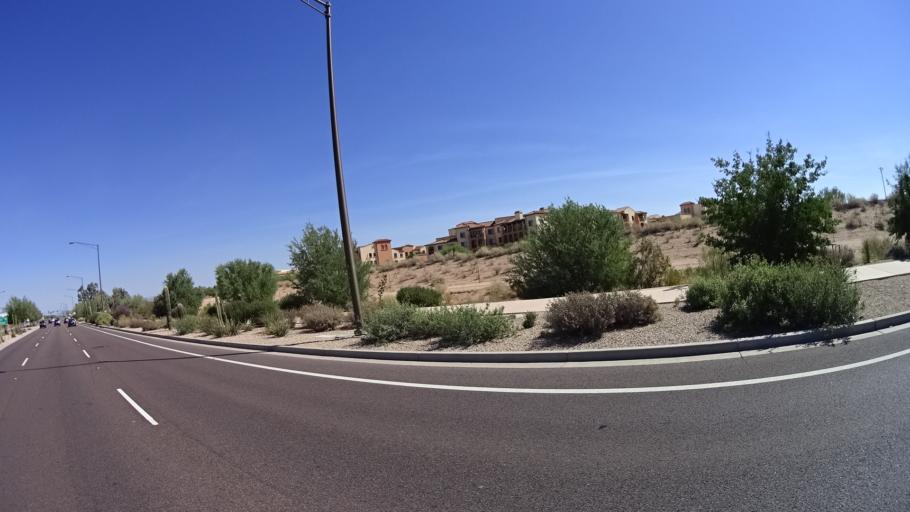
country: US
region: Arizona
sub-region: Maricopa County
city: Paradise Valley
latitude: 33.6439
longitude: -111.9251
